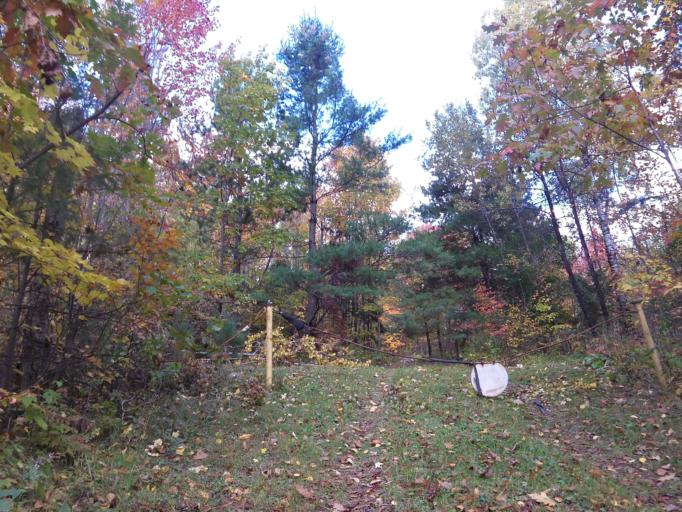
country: CA
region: Ontario
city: Petawawa
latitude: 45.8123
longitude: -77.3798
